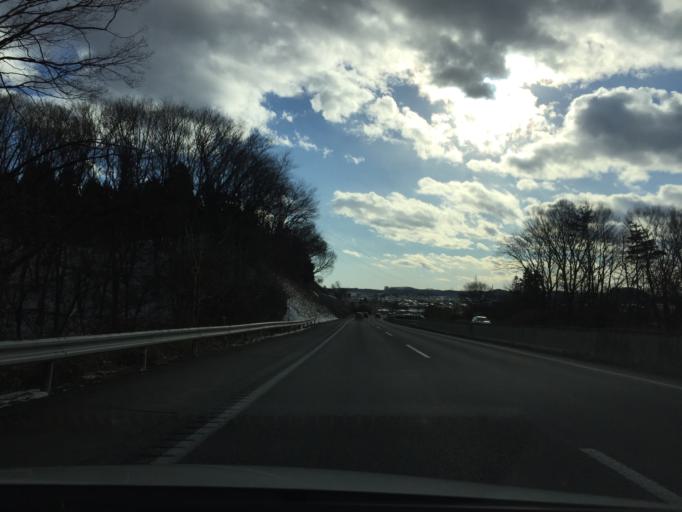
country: JP
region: Fukushima
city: Sukagawa
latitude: 37.1442
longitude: 140.2003
